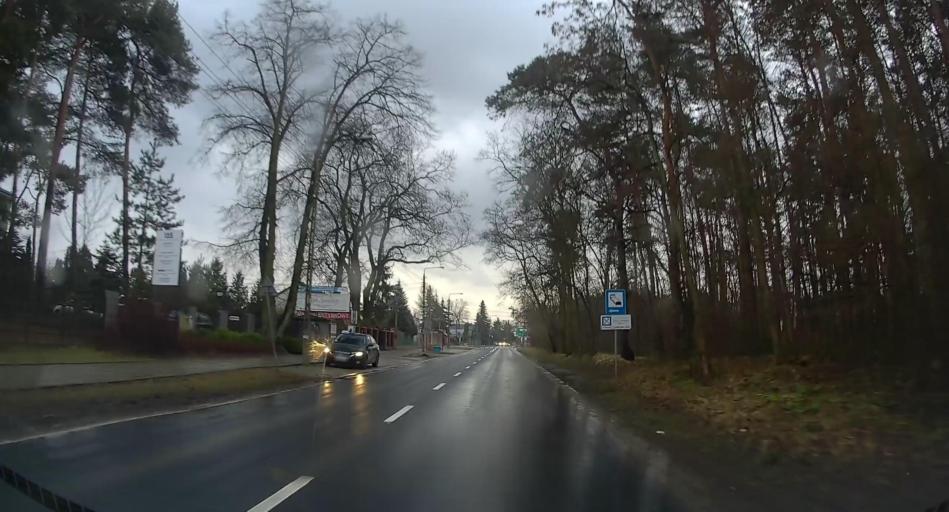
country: PL
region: Masovian Voivodeship
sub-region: Warszawa
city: Wawer
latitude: 52.1765
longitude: 21.1529
